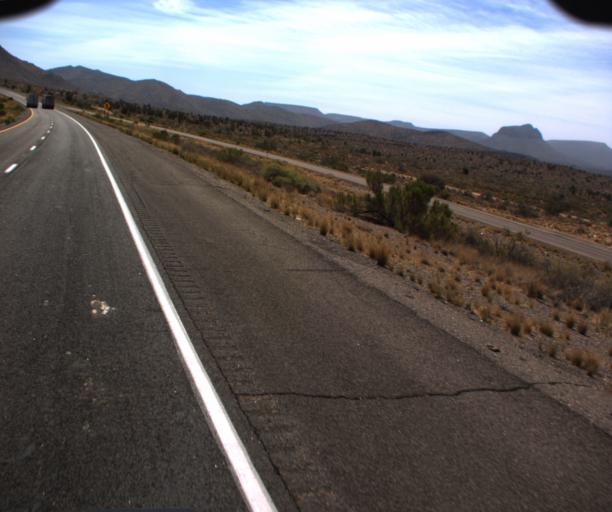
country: US
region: Arizona
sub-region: Mohave County
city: Peach Springs
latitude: 35.1594
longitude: -113.5665
